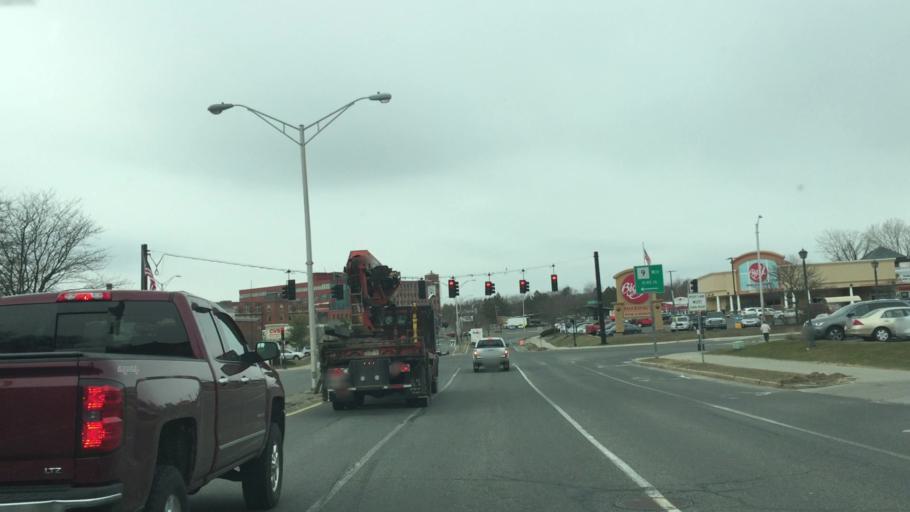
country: US
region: Massachusetts
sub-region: Berkshire County
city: Pittsfield
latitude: 42.4485
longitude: -73.2569
